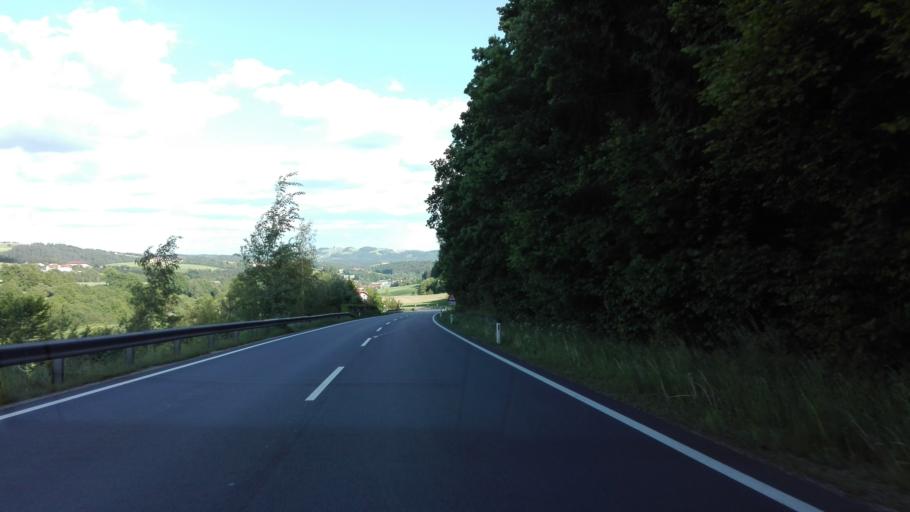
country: AT
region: Upper Austria
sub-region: Politischer Bezirk Urfahr-Umgebung
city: Engerwitzdorf
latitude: 48.3459
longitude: 14.5487
